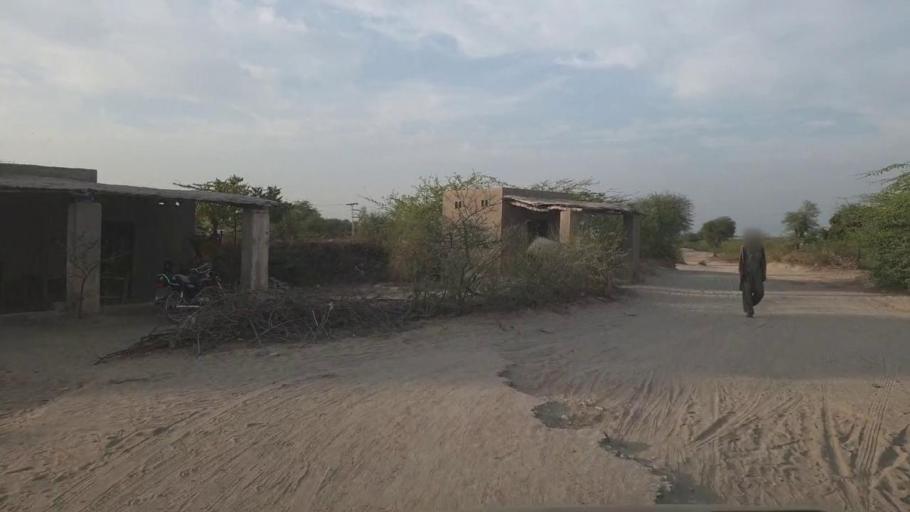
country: PK
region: Sindh
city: Nabisar
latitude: 25.1494
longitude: 69.6699
